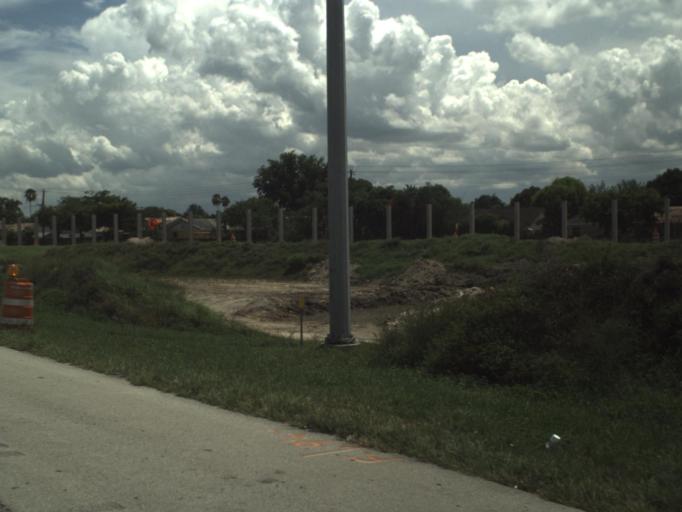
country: US
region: Florida
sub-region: Broward County
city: Southwest Ranches
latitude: 26.0598
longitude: -80.3537
